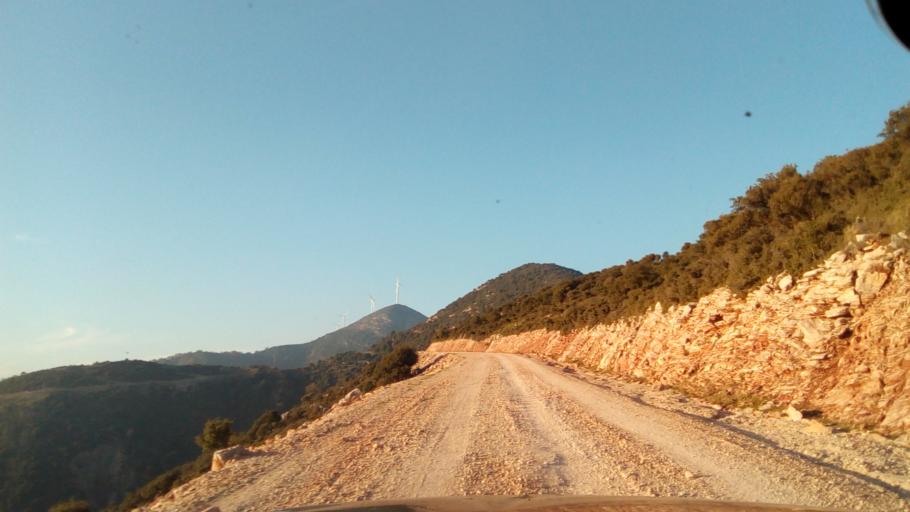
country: GR
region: West Greece
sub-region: Nomos Aitolias kai Akarnanias
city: Nafpaktos
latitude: 38.4343
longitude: 21.8496
